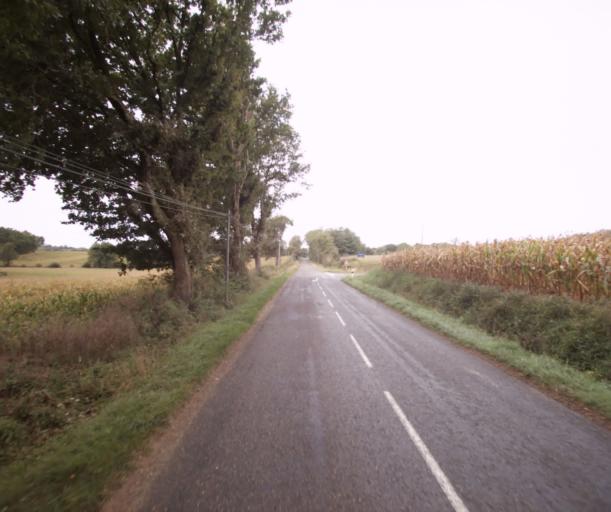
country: FR
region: Midi-Pyrenees
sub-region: Departement du Gers
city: Cazaubon
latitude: 43.8668
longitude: -0.0868
